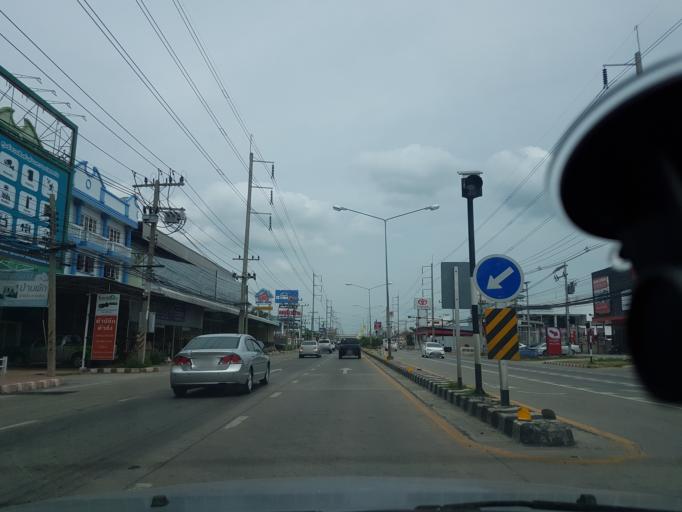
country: TH
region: Lop Buri
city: Lop Buri
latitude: 14.7856
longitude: 100.6810
